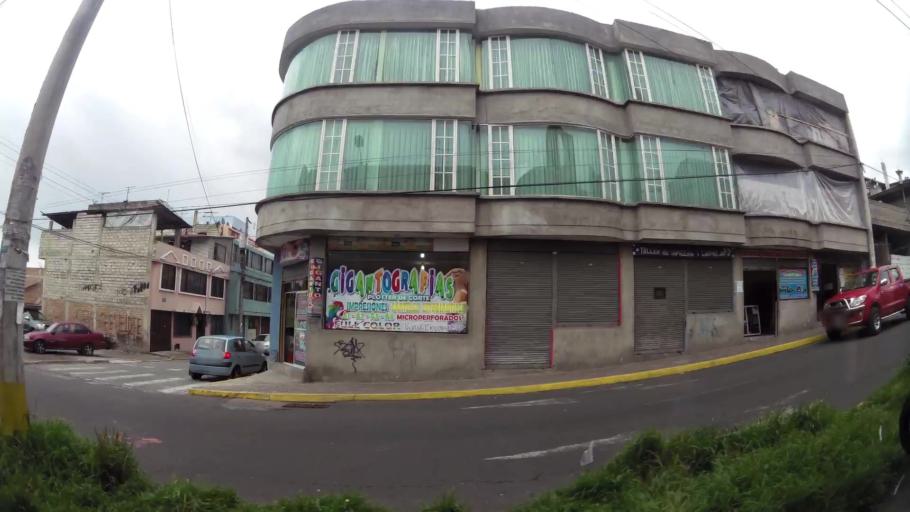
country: EC
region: Pichincha
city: Quito
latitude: -0.3211
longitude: -78.5541
